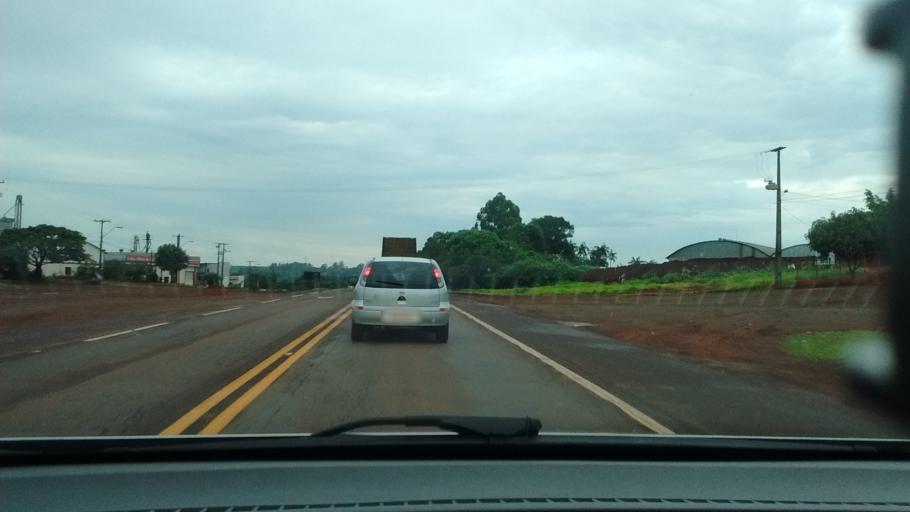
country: BR
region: Parana
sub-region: Corbelia
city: Corbelia
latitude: -24.7993
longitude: -53.2900
